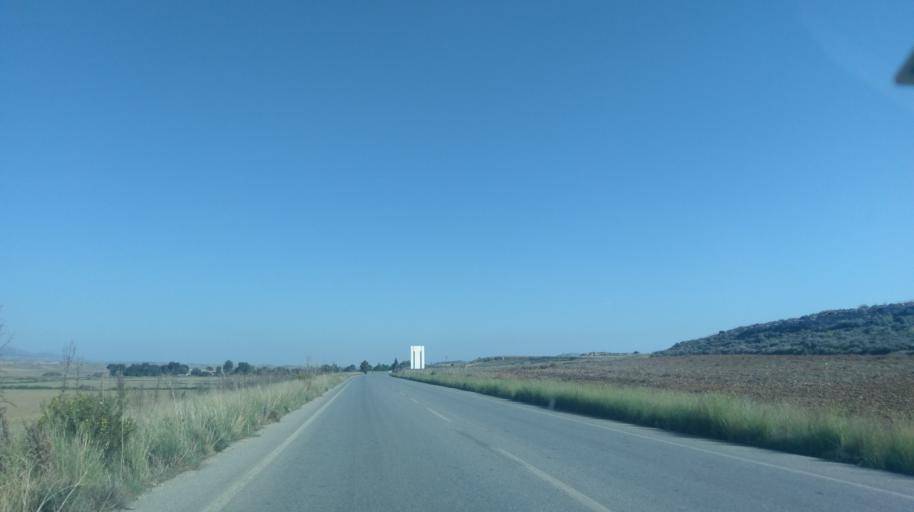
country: CY
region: Ammochostos
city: Lefkonoiko
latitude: 35.2648
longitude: 33.7989
